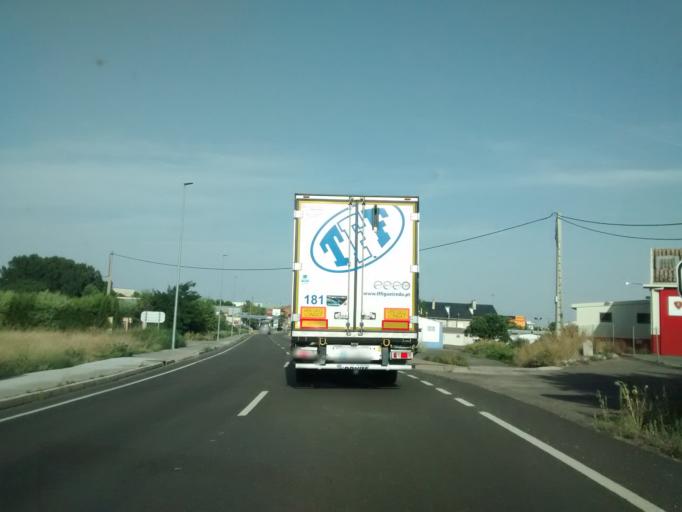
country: ES
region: Aragon
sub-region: Provincia de Zaragoza
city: Borja
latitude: 41.8320
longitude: -1.5241
